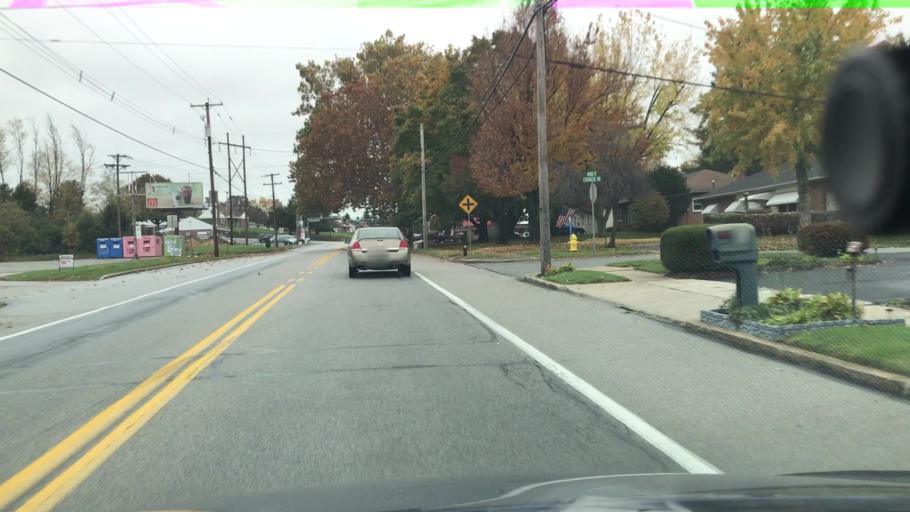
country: US
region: Pennsylvania
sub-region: York County
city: Spring Grove
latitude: 39.9088
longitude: -76.8432
